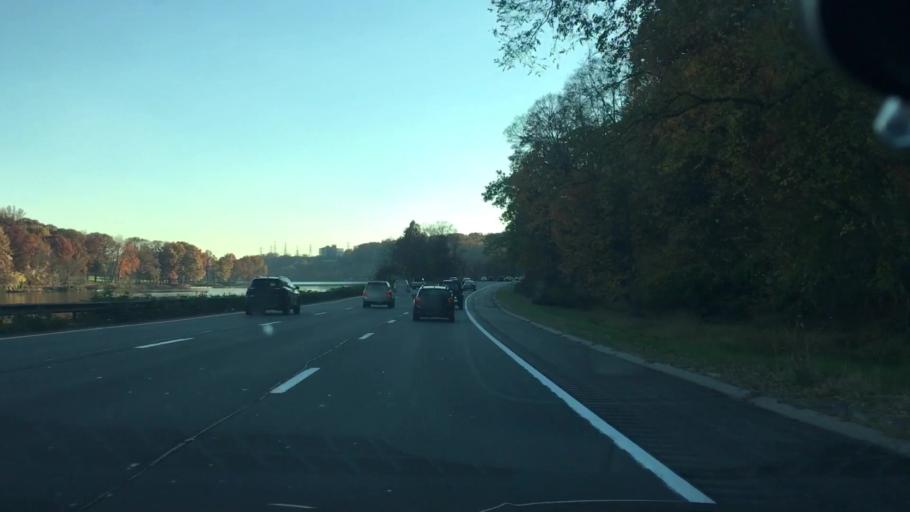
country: US
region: New York
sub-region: Westchester County
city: Greenville
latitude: 40.9801
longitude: -73.8476
